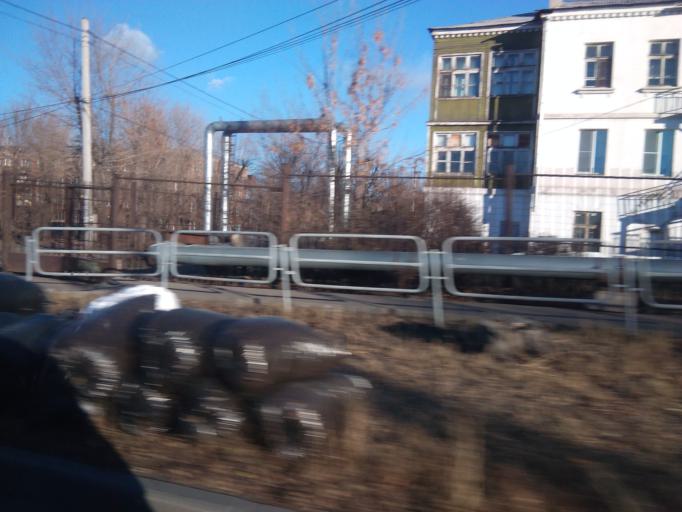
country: RU
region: Chelyabinsk
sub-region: Gorod Magnitogorsk
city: Magnitogorsk
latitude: 53.3888
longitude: 59.0524
